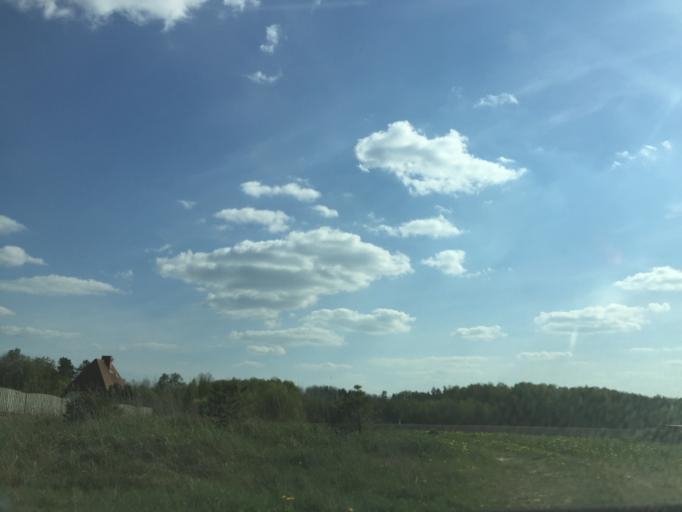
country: LV
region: Vecumnieki
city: Vecumnieki
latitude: 56.5397
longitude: 24.4157
